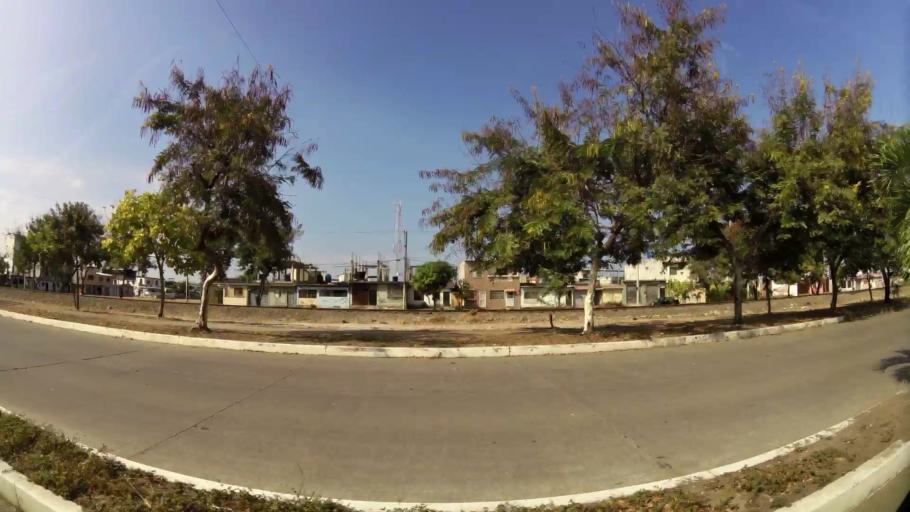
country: EC
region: Guayas
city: Eloy Alfaro
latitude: -2.1704
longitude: -79.8004
